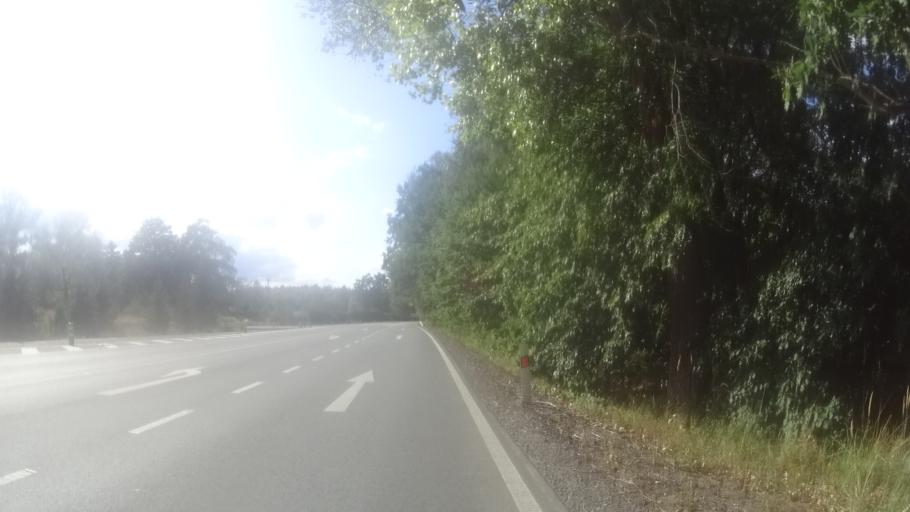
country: CZ
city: Borohradek
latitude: 50.1035
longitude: 16.0847
